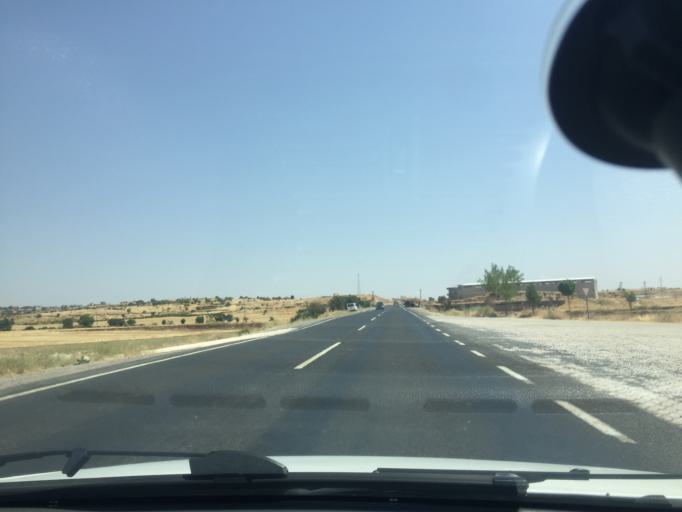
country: TR
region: Mardin
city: Acirli
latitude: 37.4481
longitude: 41.2739
